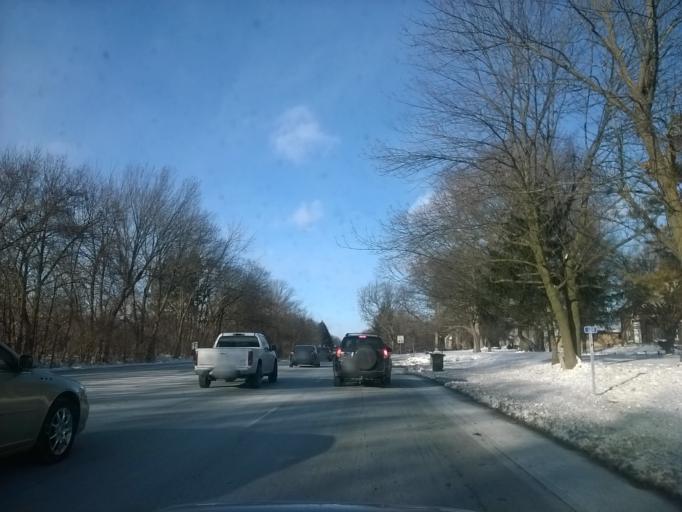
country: US
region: Indiana
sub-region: Marion County
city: Meridian Hills
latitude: 39.8804
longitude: -86.1578
